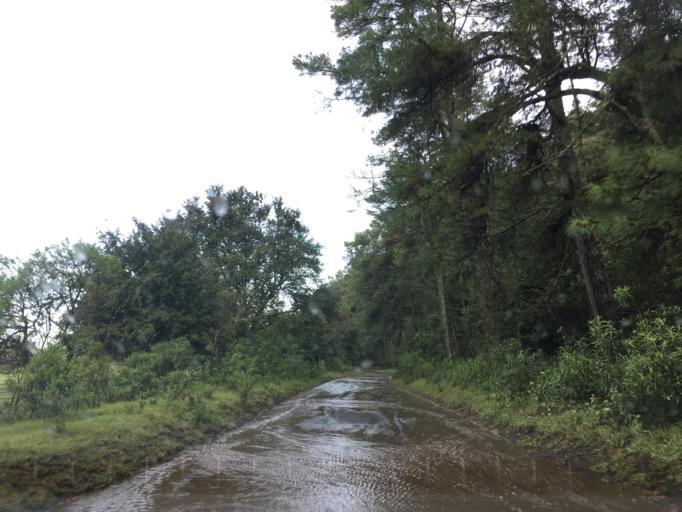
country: MX
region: Michoacan
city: Angahuan
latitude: 19.5103
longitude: -102.2141
